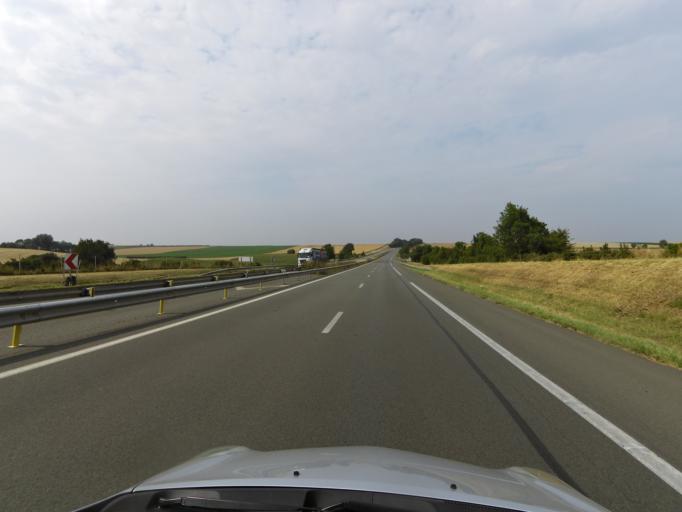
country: FR
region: Picardie
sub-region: Departement de la Somme
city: Epehy
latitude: 50.0089
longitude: 3.1741
